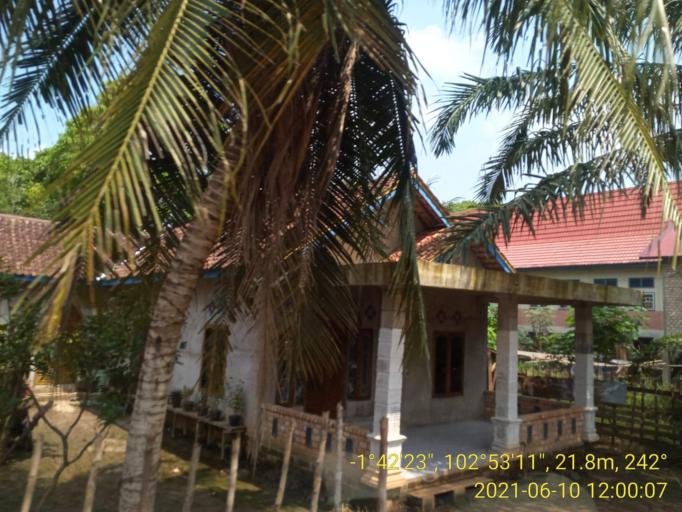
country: ID
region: Jambi
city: Mersam
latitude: -1.7066
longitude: 102.8866
